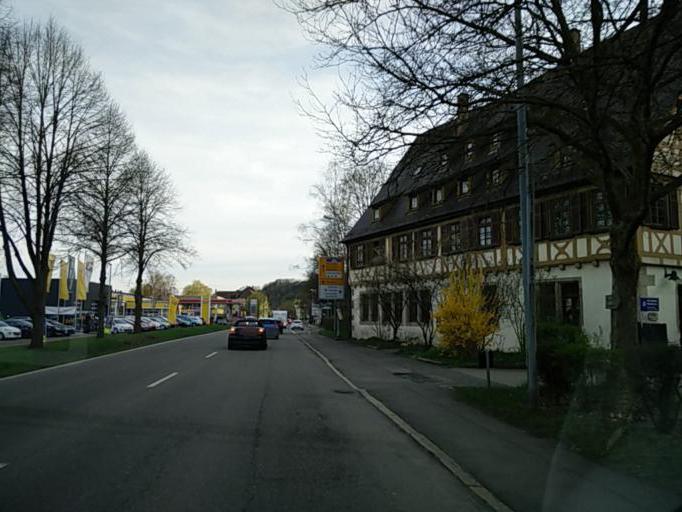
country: DE
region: Baden-Wuerttemberg
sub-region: Tuebingen Region
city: Tuebingen
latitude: 48.5342
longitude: 9.0773
